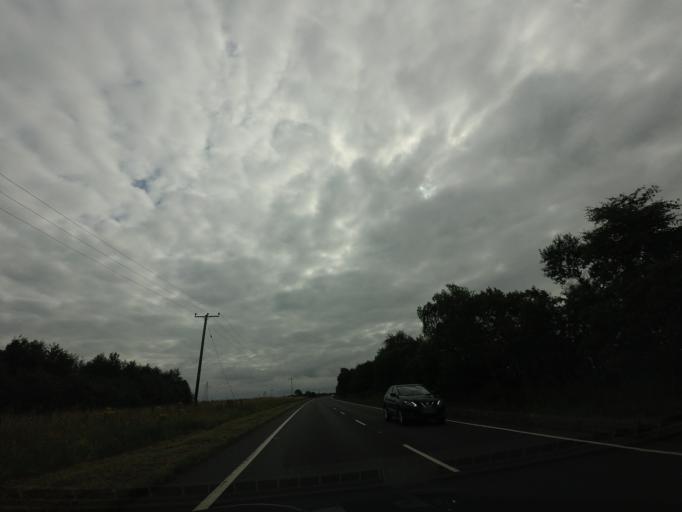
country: GB
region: Scotland
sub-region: Dumfries and Galloway
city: Annan
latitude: 54.9920
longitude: -3.1733
